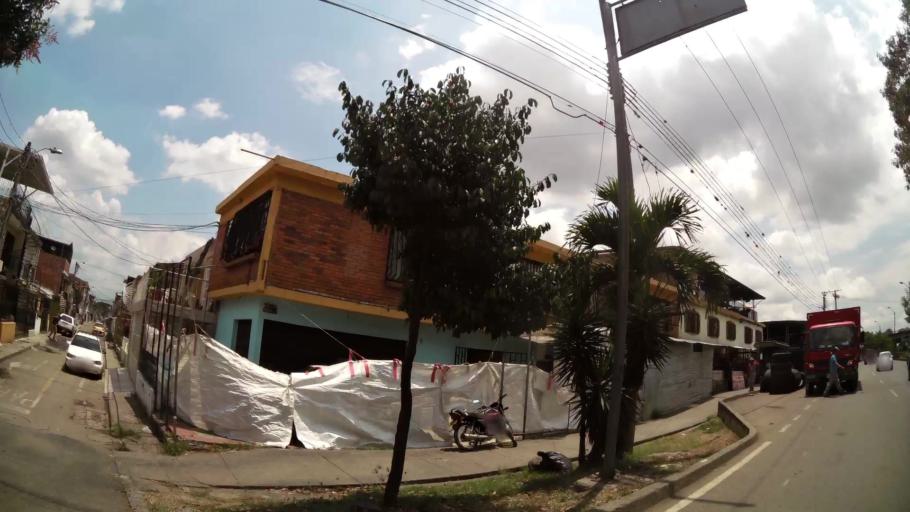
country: CO
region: Valle del Cauca
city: Cali
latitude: 3.4530
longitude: -76.4823
